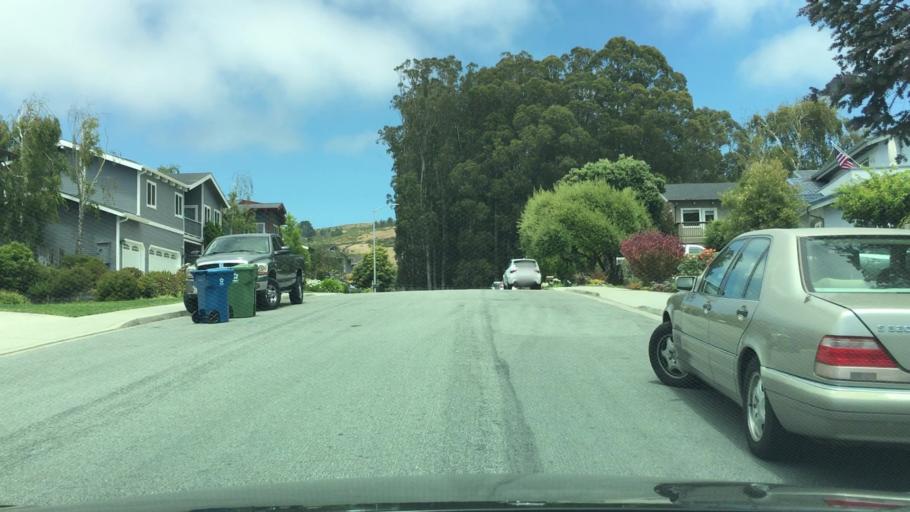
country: US
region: California
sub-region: San Mateo County
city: Half Moon Bay
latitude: 37.4752
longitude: -122.4307
